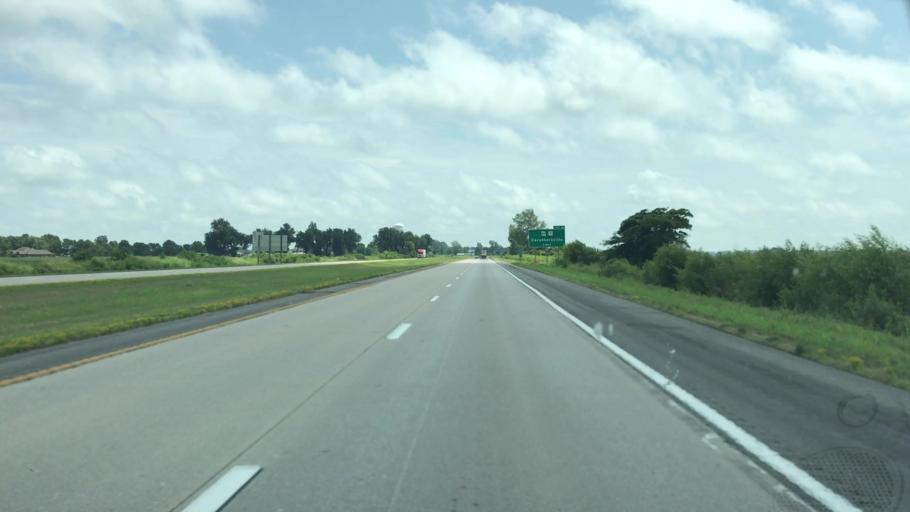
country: US
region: Missouri
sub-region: Pemiscot County
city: Caruthersville
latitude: 36.1635
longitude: -89.6809
